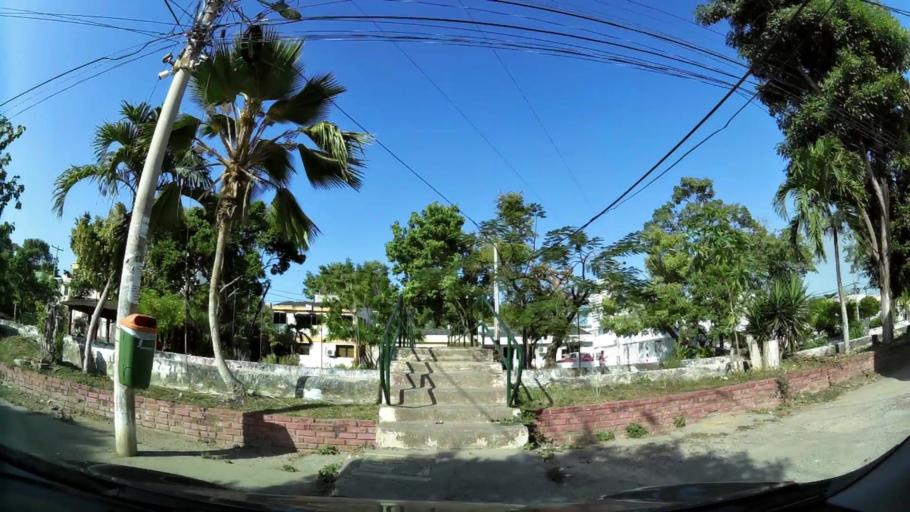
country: CO
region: Bolivar
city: Cartagena
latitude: 10.3915
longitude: -75.4826
